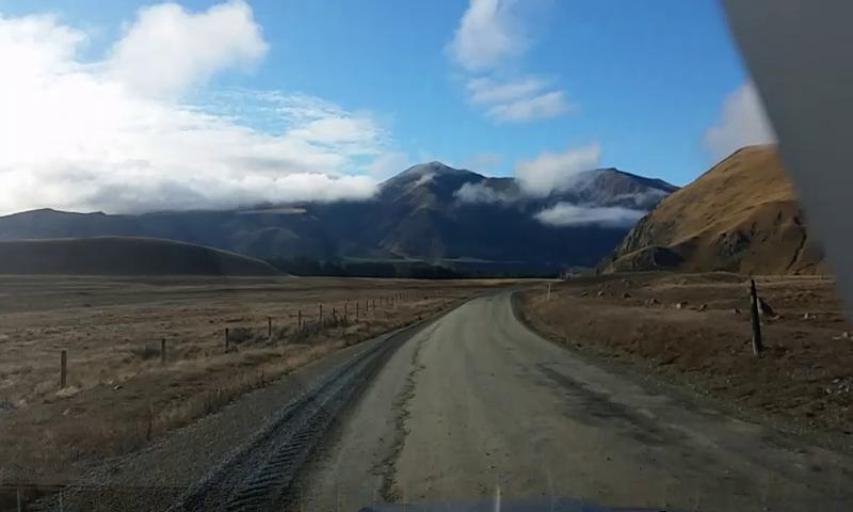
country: NZ
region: Canterbury
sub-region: Ashburton District
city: Methven
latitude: -43.6143
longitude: 171.1507
